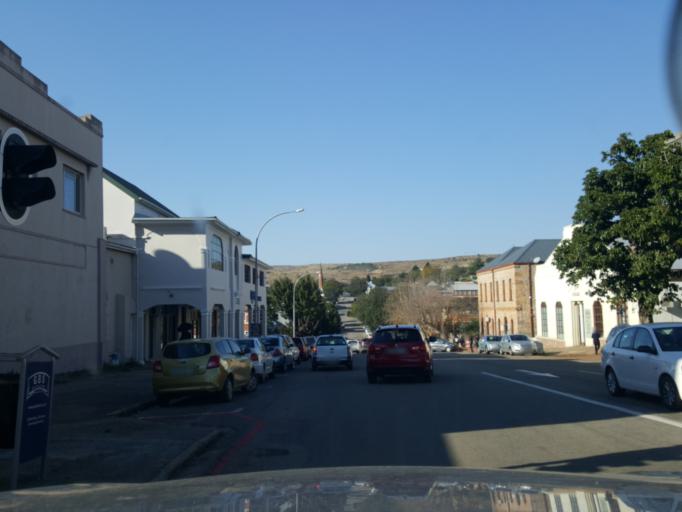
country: ZA
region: Eastern Cape
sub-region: Cacadu District Municipality
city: Grahamstown
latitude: -33.3103
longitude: 26.5267
